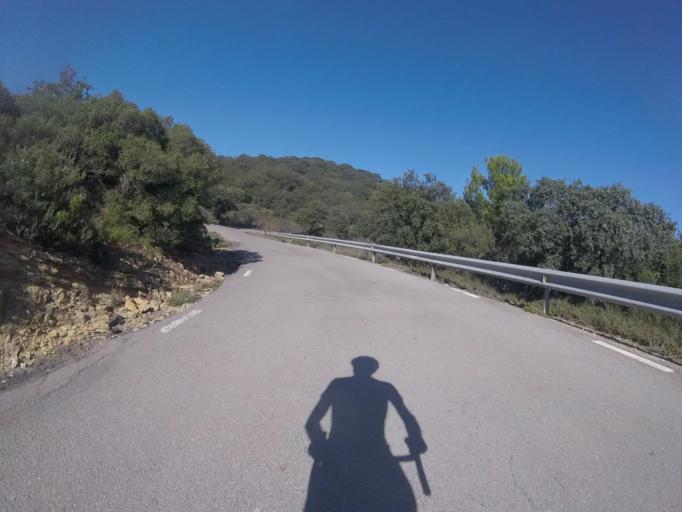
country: ES
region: Valencia
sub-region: Provincia de Castello
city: Sarratella
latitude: 40.3047
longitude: 0.0310
